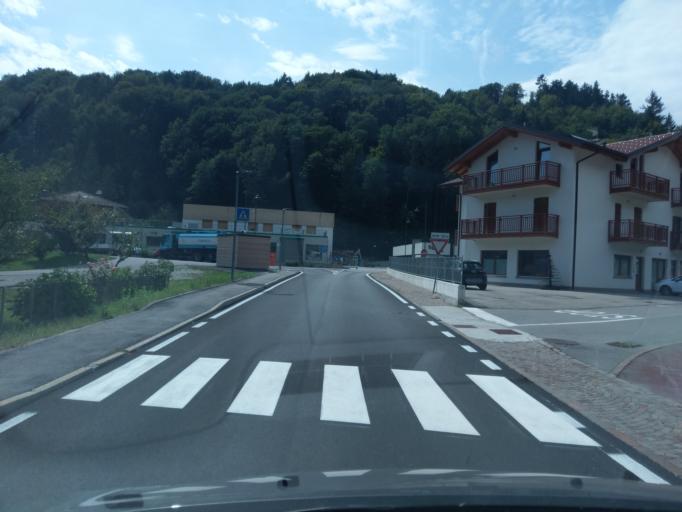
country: IT
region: Trentino-Alto Adige
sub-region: Provincia di Trento
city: Ponte Arche
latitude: 46.0370
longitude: 10.8637
